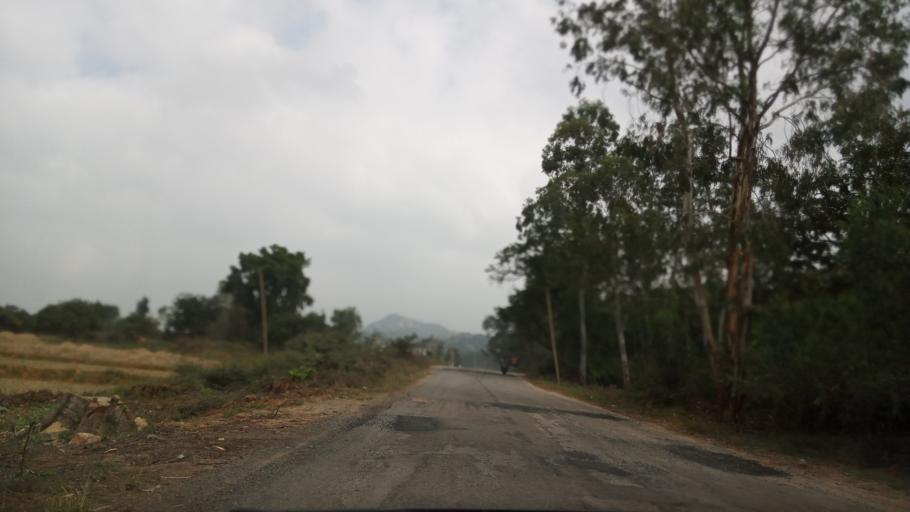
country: IN
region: Andhra Pradesh
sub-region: Chittoor
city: Madanapalle
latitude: 13.5019
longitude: 78.3304
